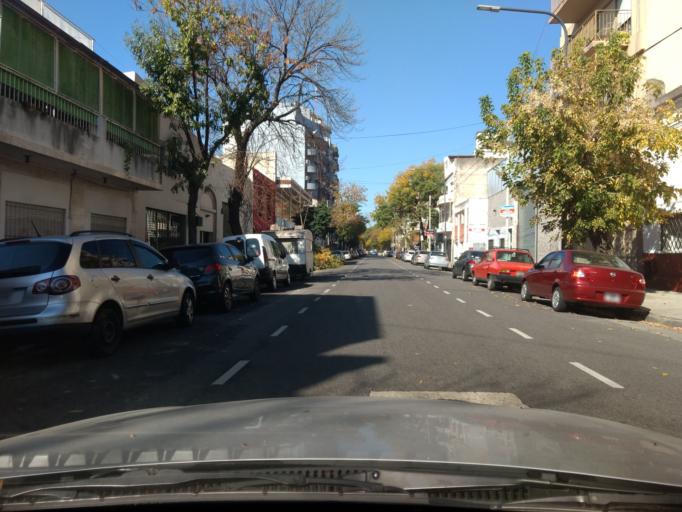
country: AR
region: Buenos Aires F.D.
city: Villa Santa Rita
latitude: -34.6373
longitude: -58.4850
